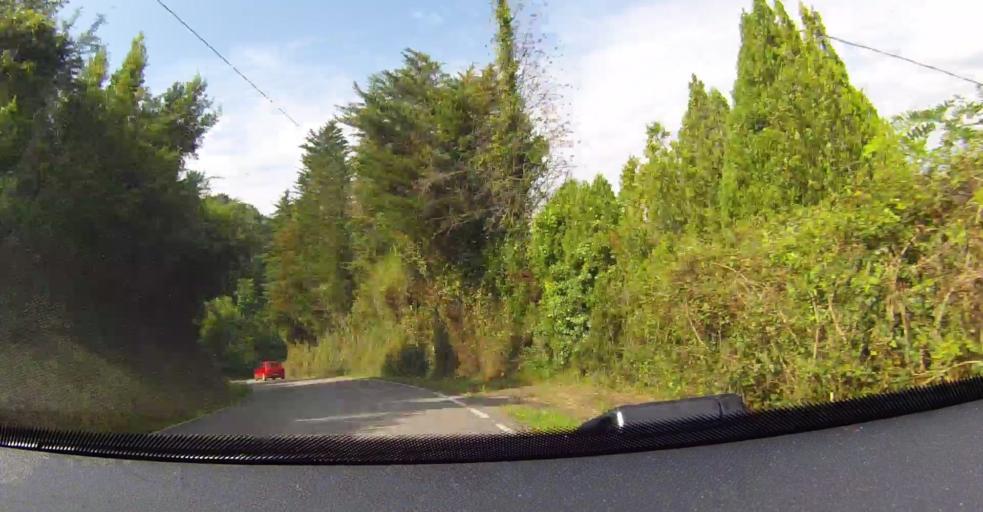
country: ES
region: Asturias
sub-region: Province of Asturias
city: Villaviciosa
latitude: 43.4851
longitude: -5.4212
